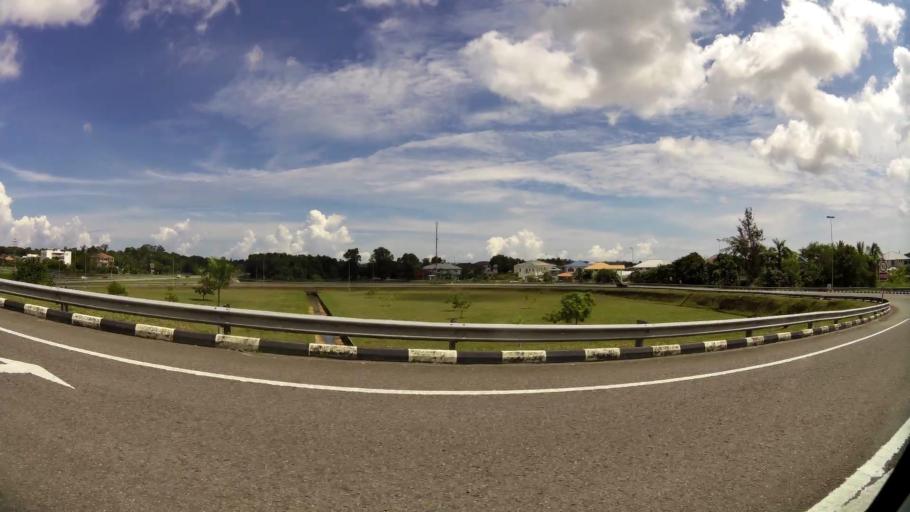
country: BN
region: Brunei and Muara
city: Bandar Seri Begawan
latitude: 4.9430
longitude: 114.9099
